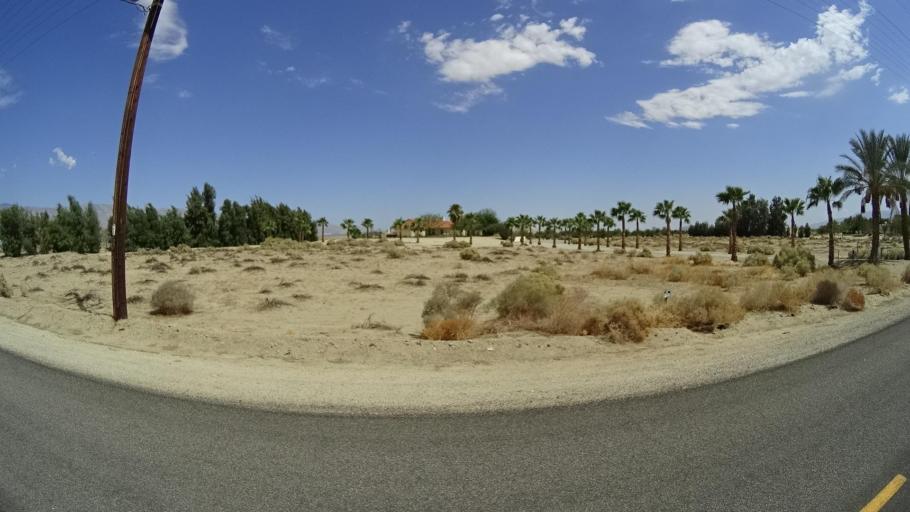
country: US
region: California
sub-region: San Diego County
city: Borrego Springs
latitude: 33.2690
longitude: -116.3485
